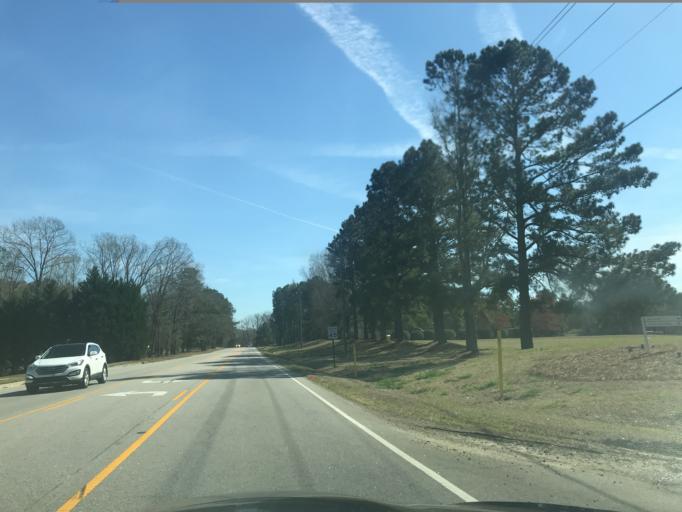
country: US
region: North Carolina
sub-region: Wake County
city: Fuquay-Varina
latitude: 35.5773
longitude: -78.7709
